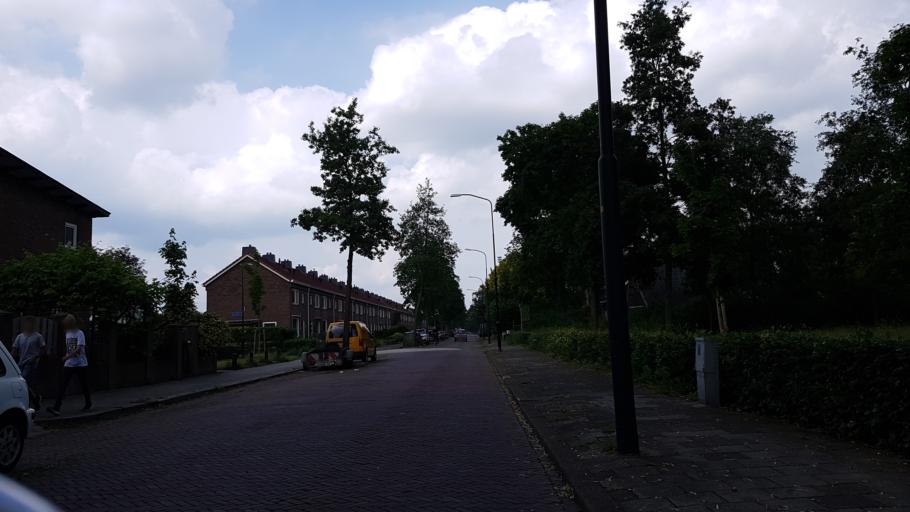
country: NL
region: Gelderland
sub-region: Gemeente Apeldoorn
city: Apeldoorn
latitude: 52.1885
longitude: 5.9701
